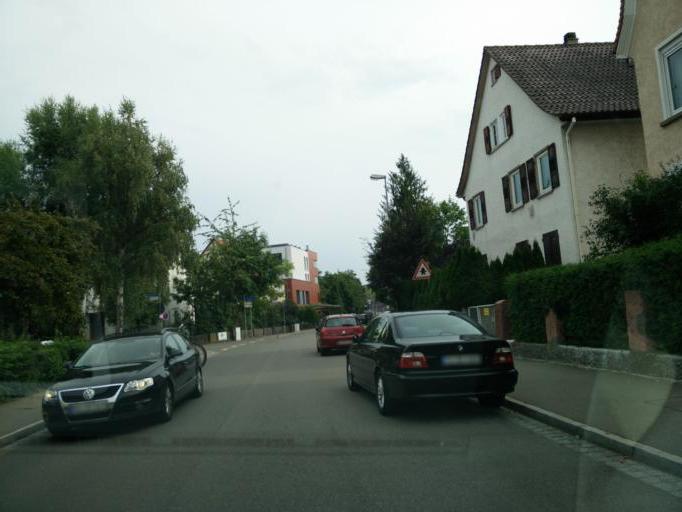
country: DE
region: Baden-Wuerttemberg
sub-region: Tuebingen Region
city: Tuebingen
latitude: 48.5127
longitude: 9.0517
